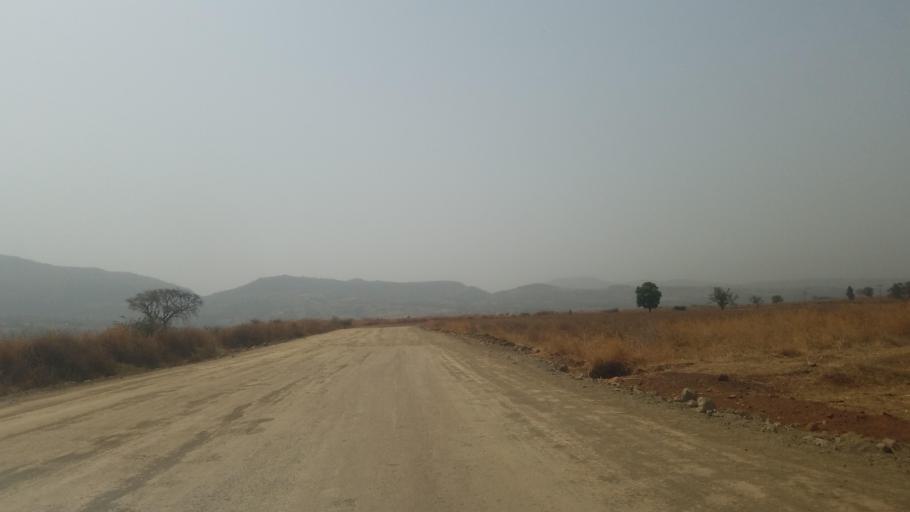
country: ET
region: Amhara
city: Bure
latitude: 10.9012
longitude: 36.4657
